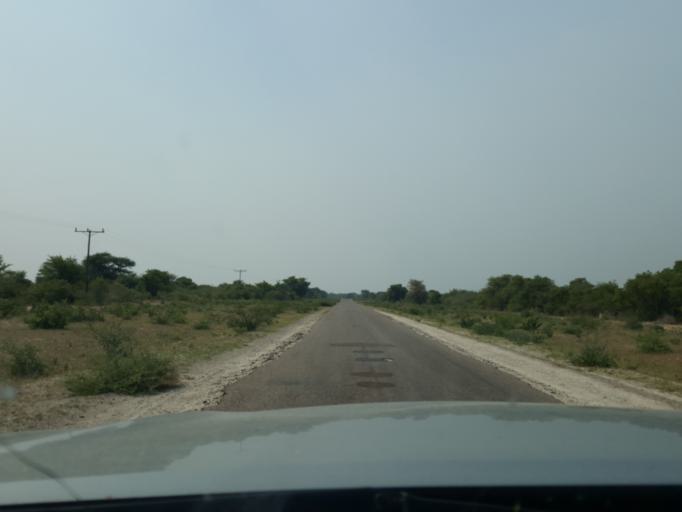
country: BW
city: Nokaneng
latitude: -19.1042
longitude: 22.2710
